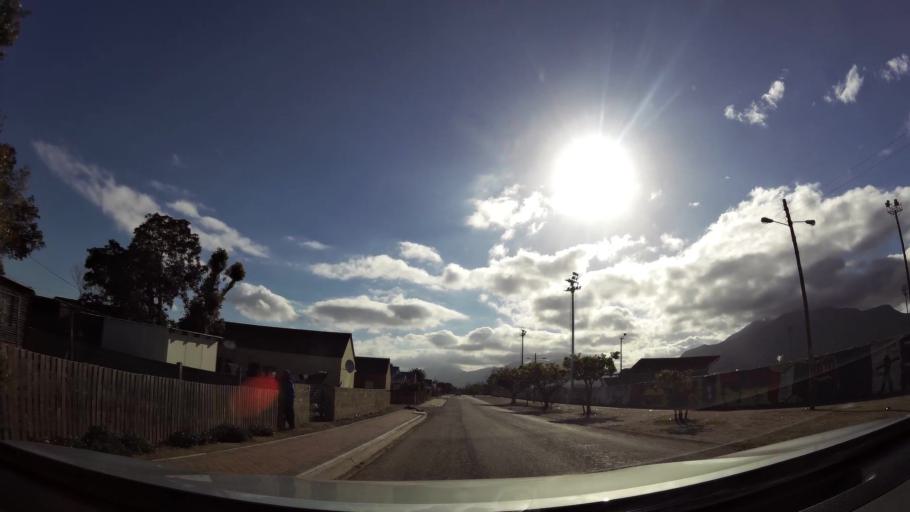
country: ZA
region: Western Cape
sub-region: Eden District Municipality
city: George
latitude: -33.9711
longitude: 22.4809
